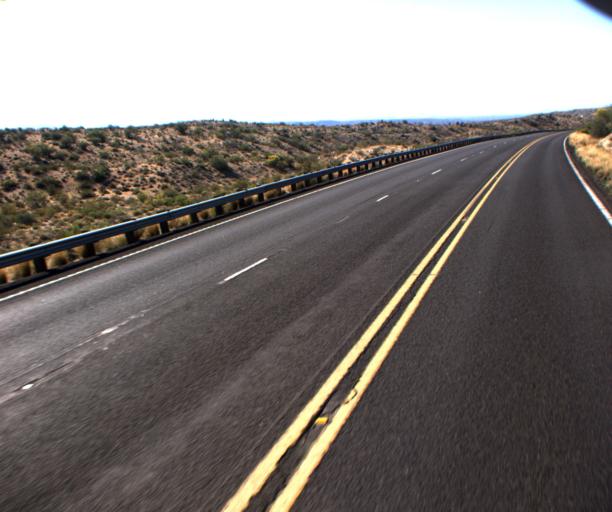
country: US
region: Arizona
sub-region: Mohave County
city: Kingman
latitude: 34.9299
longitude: -113.6593
